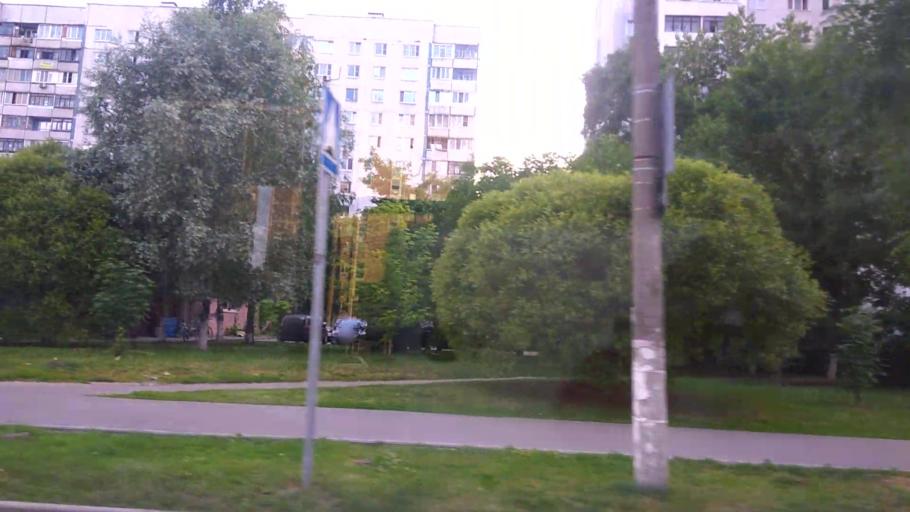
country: RU
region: Moskovskaya
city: Yubileyny
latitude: 55.9213
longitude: 37.8685
